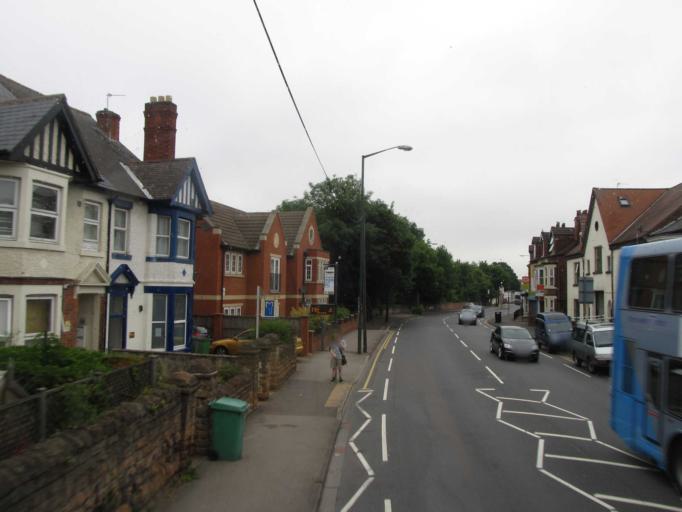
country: GB
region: England
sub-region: Nottinghamshire
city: Arnold
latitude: 52.9776
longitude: -1.1360
